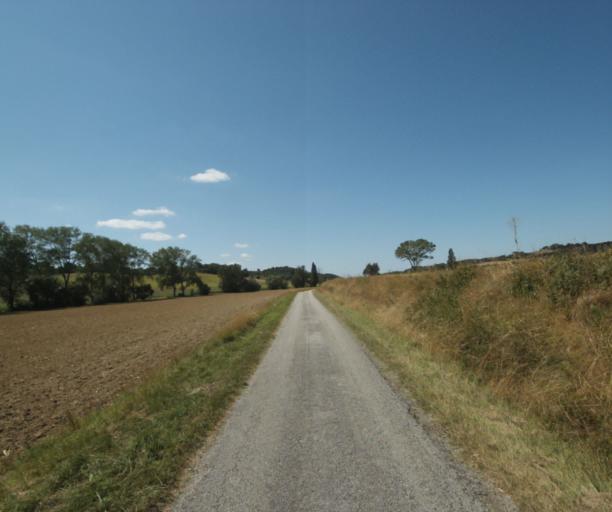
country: FR
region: Midi-Pyrenees
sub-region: Departement de la Haute-Garonne
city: Saint-Felix-Lauragais
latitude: 43.4916
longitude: 1.8708
